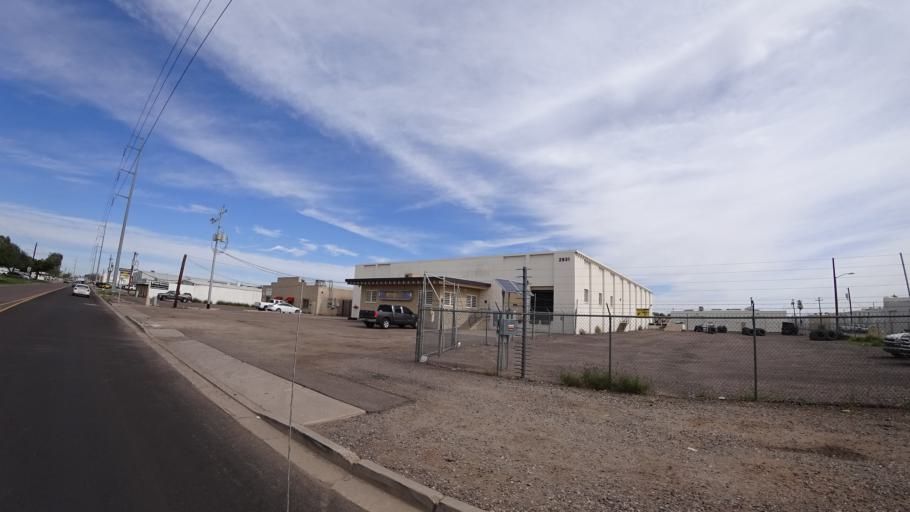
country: US
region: Arizona
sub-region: Maricopa County
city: Phoenix
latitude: 33.4812
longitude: -112.1257
